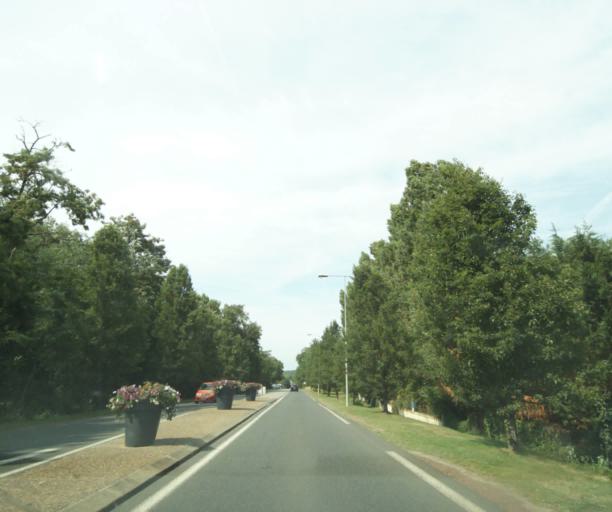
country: FR
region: Centre
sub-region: Departement d'Indre-et-Loire
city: Montbazon
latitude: 47.2800
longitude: 0.7112
